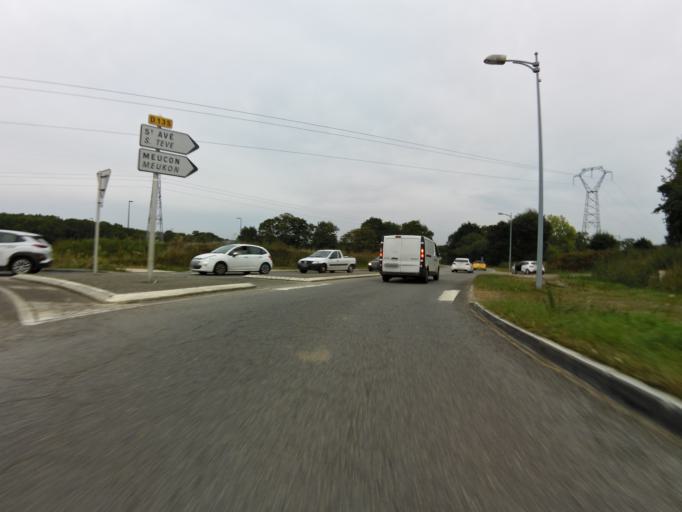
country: FR
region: Brittany
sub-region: Departement du Morbihan
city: Plescop
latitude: 47.6999
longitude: -2.7961
